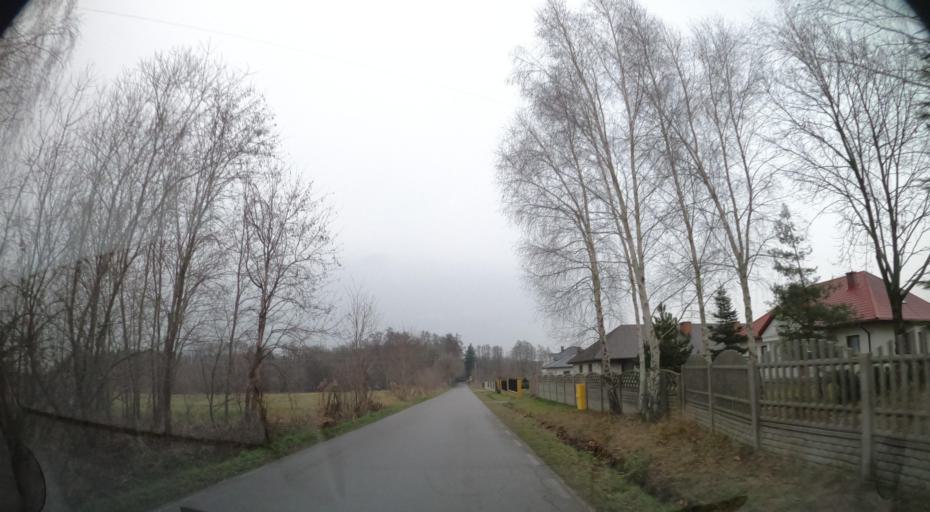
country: PL
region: Masovian Voivodeship
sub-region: Powiat radomski
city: Jastrzebia
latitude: 51.4219
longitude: 21.2263
